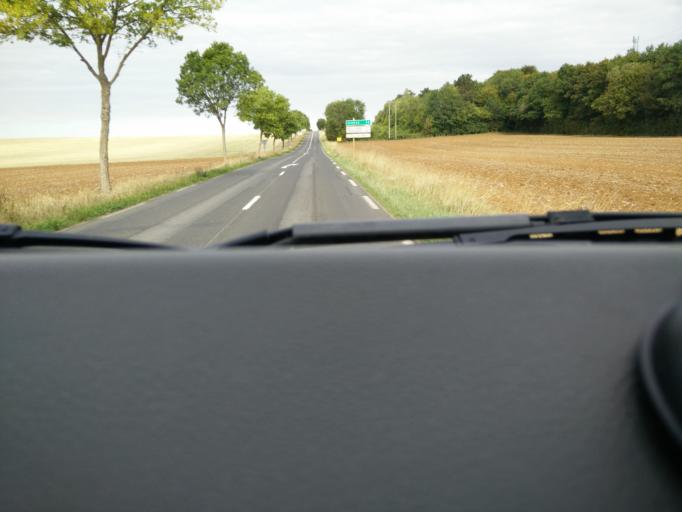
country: FR
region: Lorraine
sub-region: Departement de Meurthe-et-Moselle
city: Montauville
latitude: 48.8952
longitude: 5.9755
